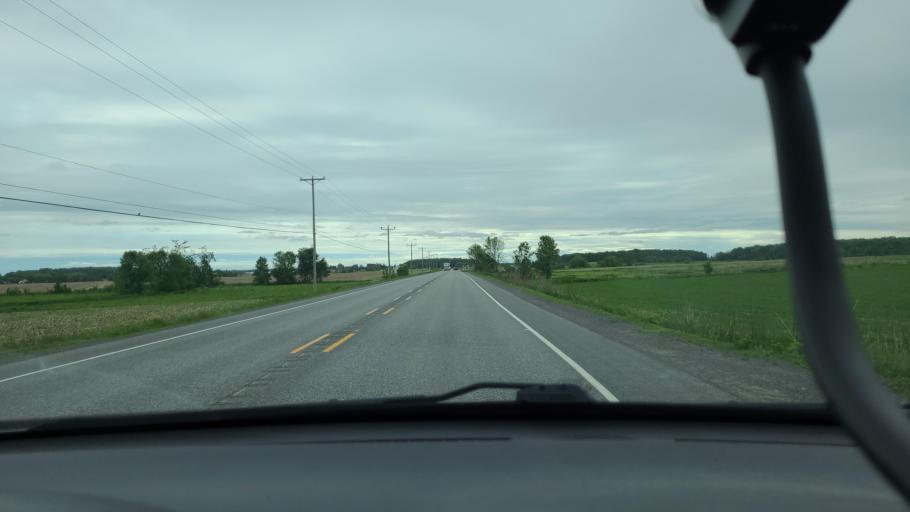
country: CA
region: Quebec
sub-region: Lanaudiere
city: Saint-Jacques
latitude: 45.9162
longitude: -73.6395
